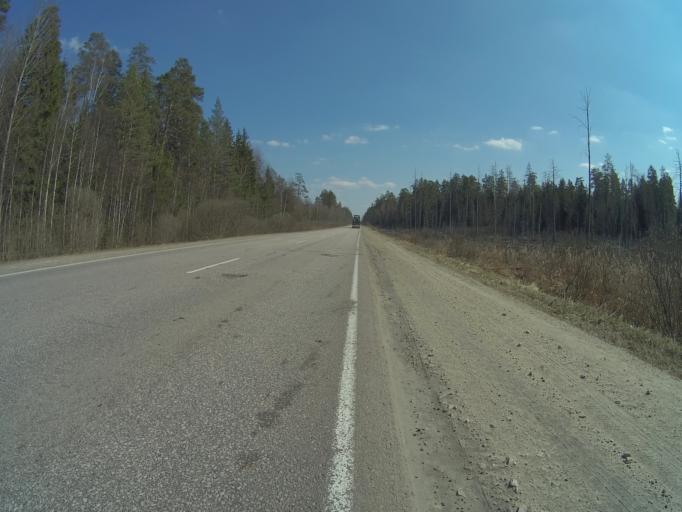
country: RU
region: Vladimir
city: Orgtrud
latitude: 56.0054
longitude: 40.6424
